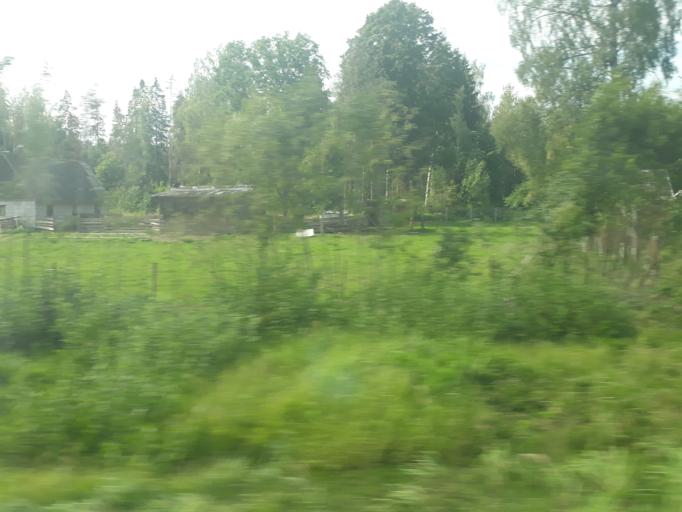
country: EE
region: Laeaene-Virumaa
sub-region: Rakke vald
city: Rakke
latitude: 58.9137
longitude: 26.2749
